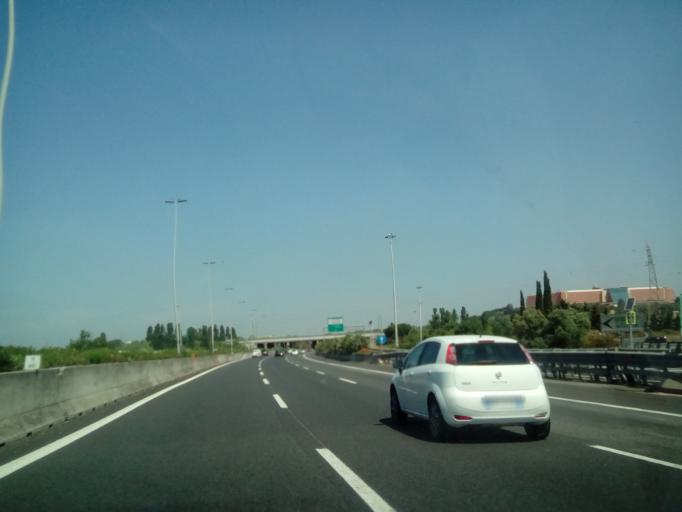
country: IT
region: Latium
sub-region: Citta metropolitana di Roma Capitale
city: Vitinia
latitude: 41.8152
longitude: 12.3934
